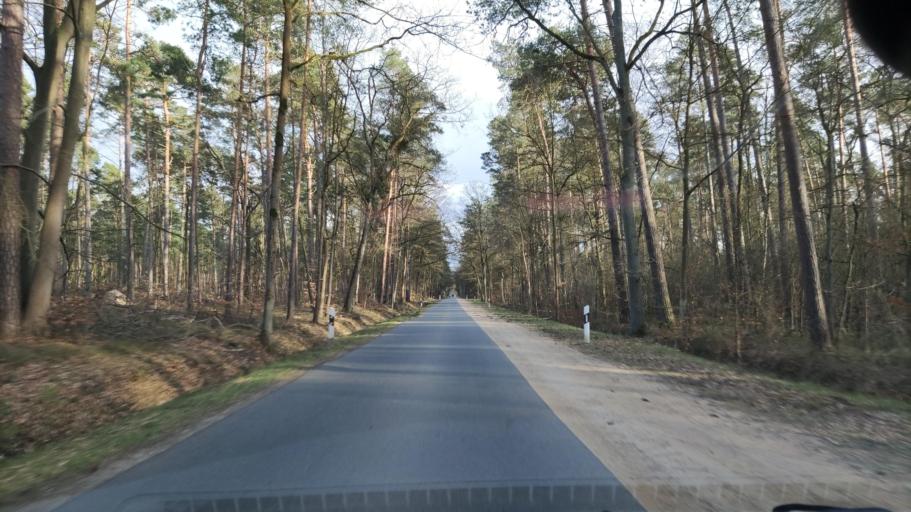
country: DE
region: Lower Saxony
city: Langendorf
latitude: 53.0399
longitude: 11.2502
